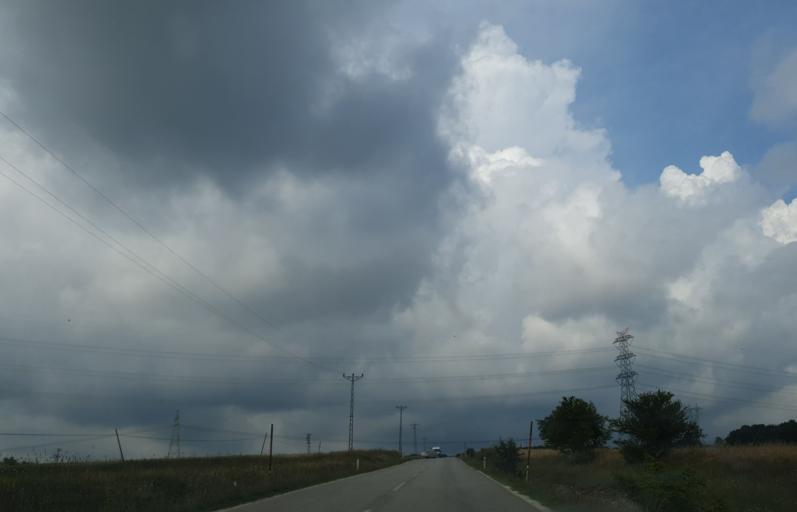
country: TR
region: Tekirdag
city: Saray
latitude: 41.4802
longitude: 27.9596
